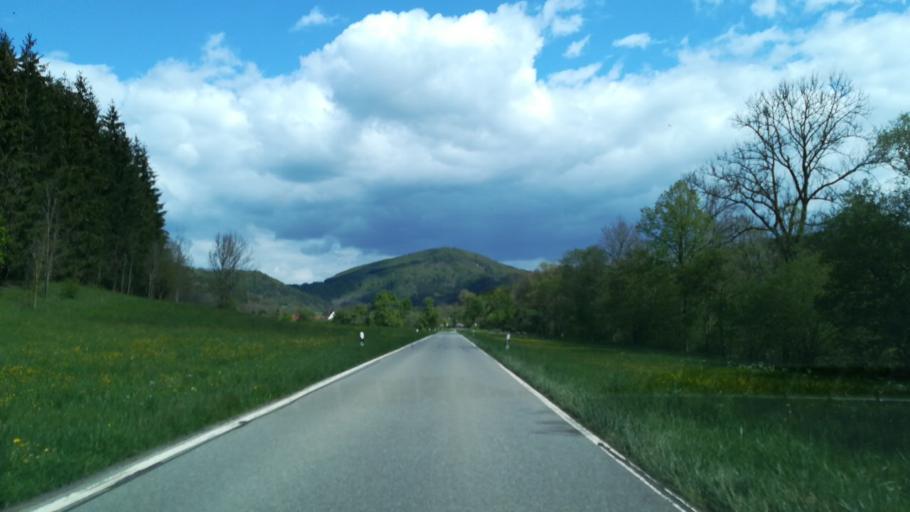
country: DE
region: Baden-Wuerttemberg
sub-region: Freiburg Region
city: Blumberg
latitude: 47.8411
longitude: 8.4795
